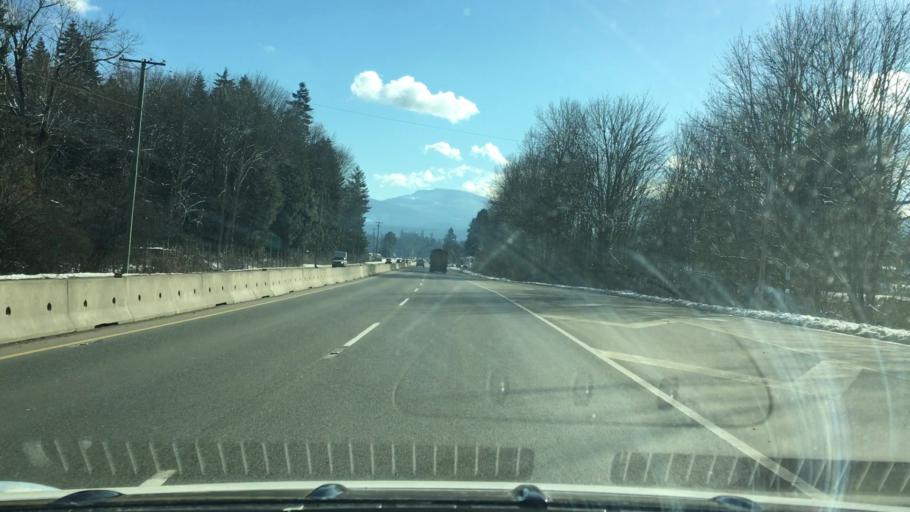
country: CA
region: British Columbia
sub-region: Cowichan Valley Regional District
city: Ladysmith
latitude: 49.0603
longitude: -123.8777
